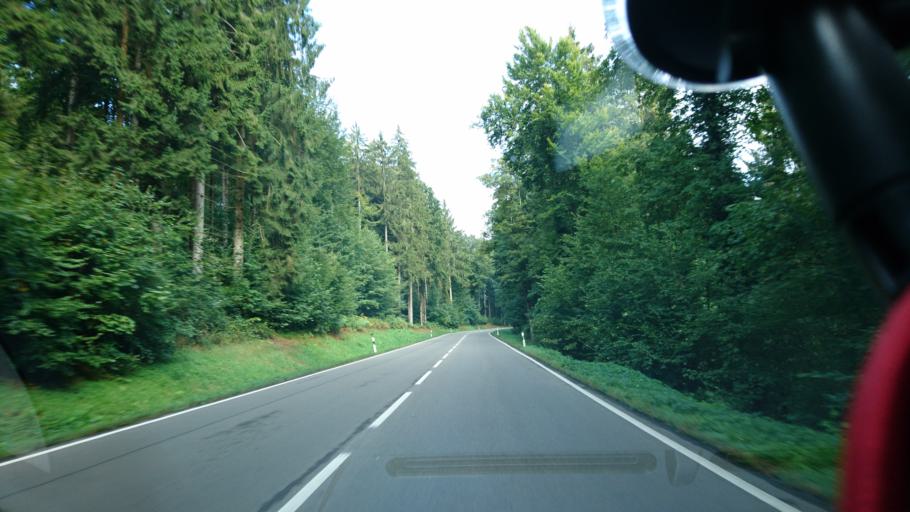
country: DE
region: Baden-Wuerttemberg
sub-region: Regierungsbezirk Stuttgart
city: Sulzbach an der Murr
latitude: 49.0254
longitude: 9.5060
